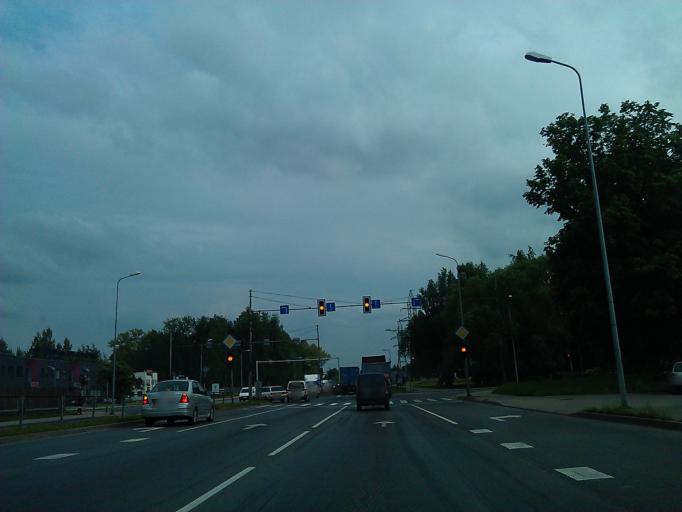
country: LV
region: Riga
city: Riga
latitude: 56.9399
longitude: 24.1716
